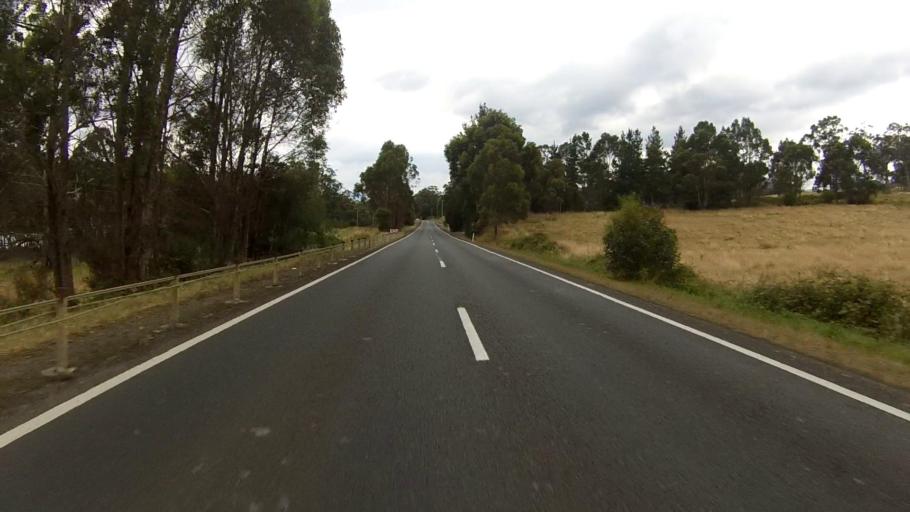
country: AU
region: Tasmania
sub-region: Huon Valley
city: Franklin
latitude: -43.0818
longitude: 147.0312
